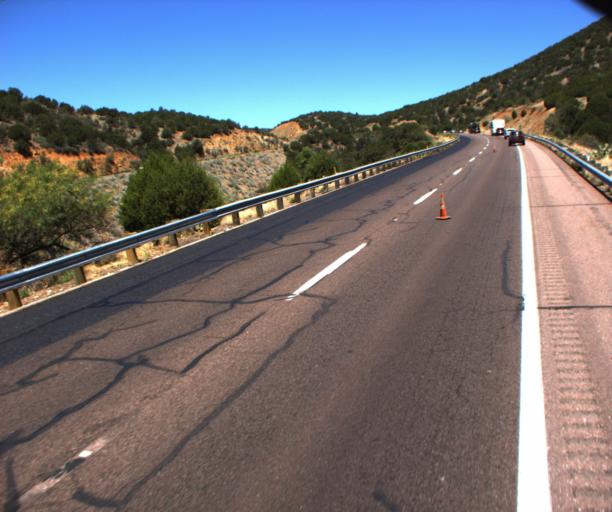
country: US
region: Arizona
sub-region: Gila County
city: Payson
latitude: 34.1609
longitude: -111.3223
